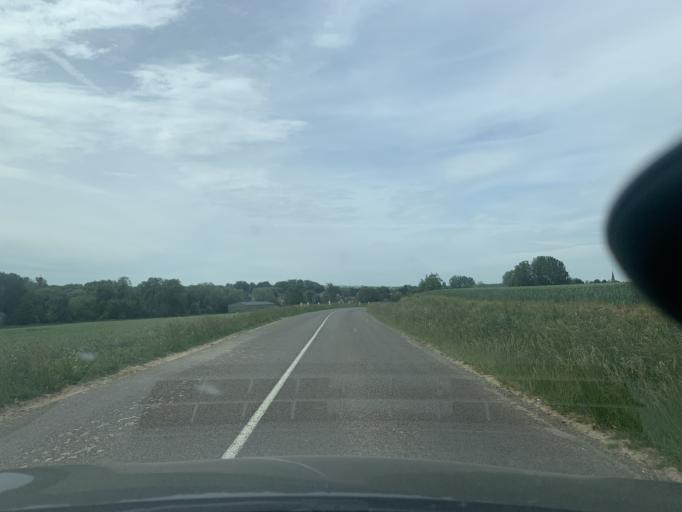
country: FR
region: Nord-Pas-de-Calais
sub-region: Departement du Nord
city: Marcoing
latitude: 50.1293
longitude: 3.1819
